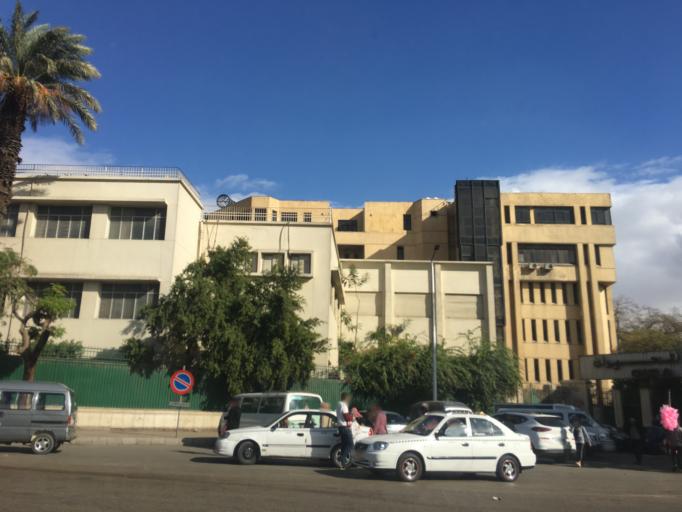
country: EG
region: Al Jizah
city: Al Jizah
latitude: 30.0249
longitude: 31.2110
